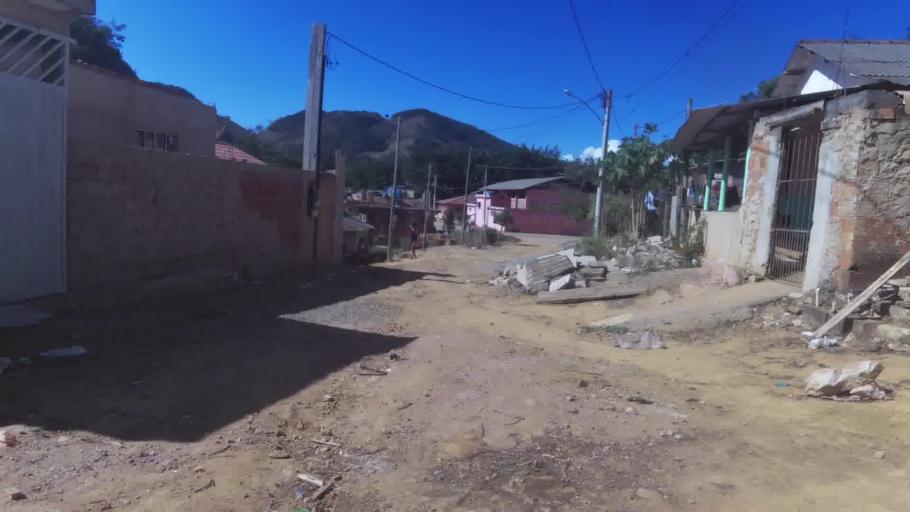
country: BR
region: Espirito Santo
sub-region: Cachoeiro De Itapemirim
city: Cachoeiro de Itapemirim
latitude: -20.9209
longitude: -41.1973
